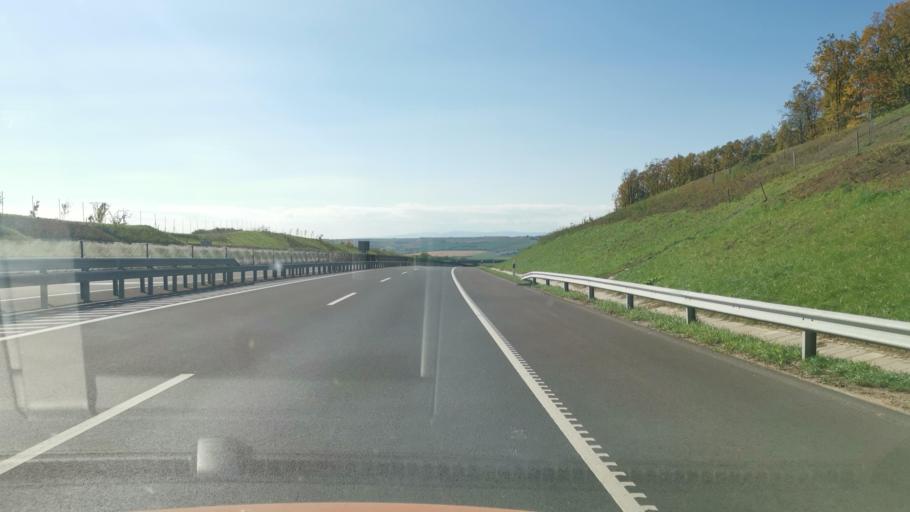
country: HU
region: Borsod-Abauj-Zemplen
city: Szikszo
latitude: 48.2177
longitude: 20.9329
